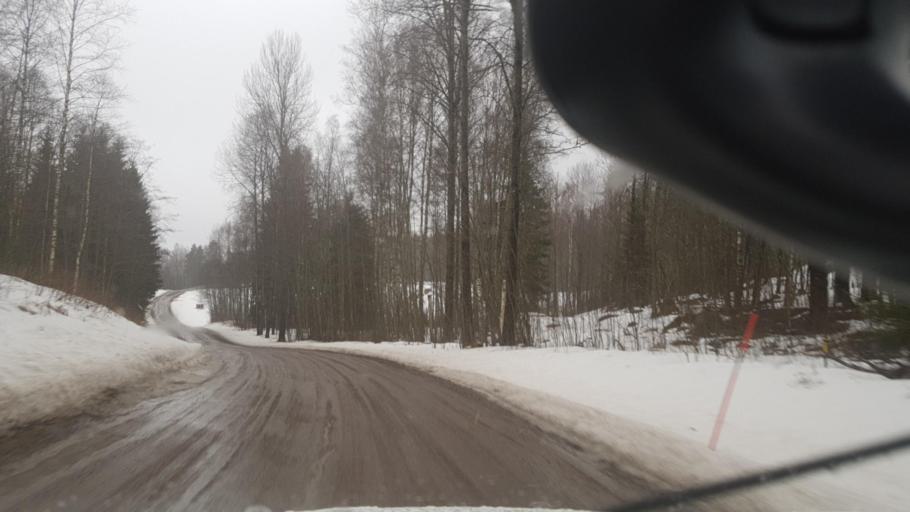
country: SE
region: Vaermland
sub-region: Eda Kommun
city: Amotfors
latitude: 59.8110
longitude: 12.3616
